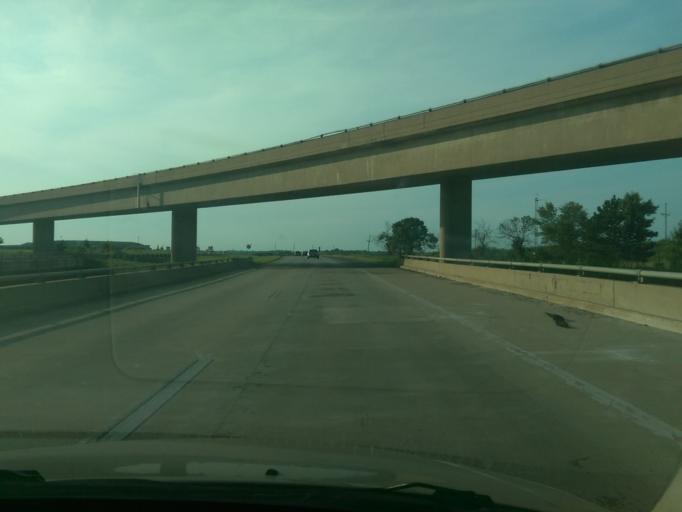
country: US
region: Missouri
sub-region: Platte County
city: Weatherby Lake
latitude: 39.3109
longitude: -94.6878
